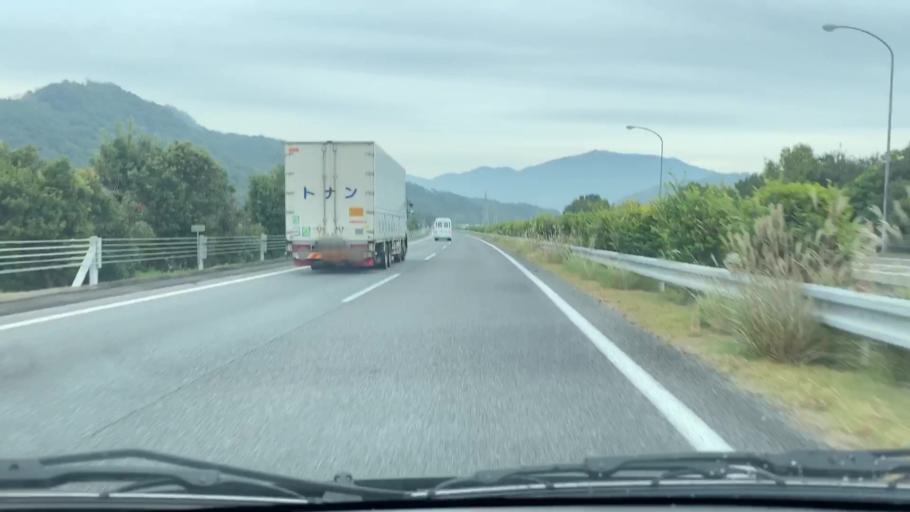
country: JP
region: Saga Prefecture
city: Takeocho-takeo
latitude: 33.2544
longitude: 130.0791
